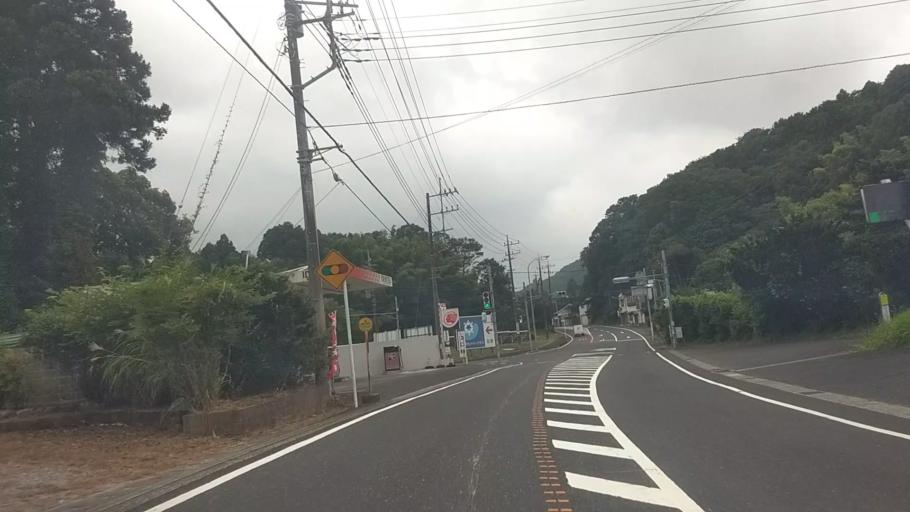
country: JP
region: Chiba
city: Kawaguchi
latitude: 35.2287
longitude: 140.0755
